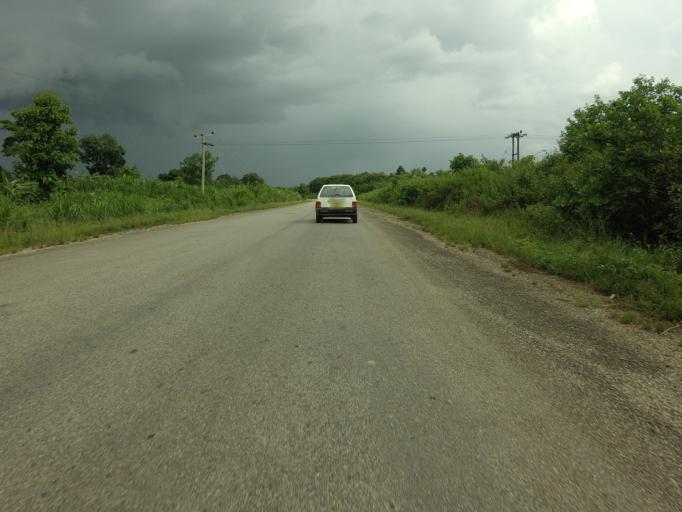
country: TG
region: Plateaux
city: Badou
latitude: 7.6764
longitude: 0.5197
